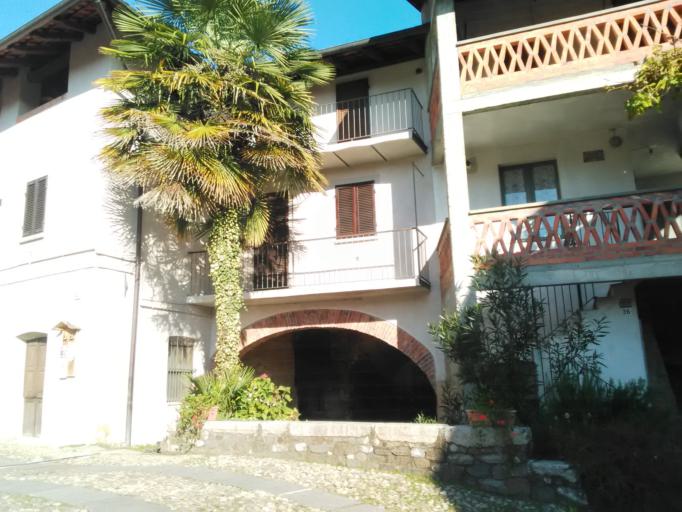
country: IT
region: Piedmont
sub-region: Provincia di Vercelli
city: Postua
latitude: 45.7157
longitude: 8.2280
